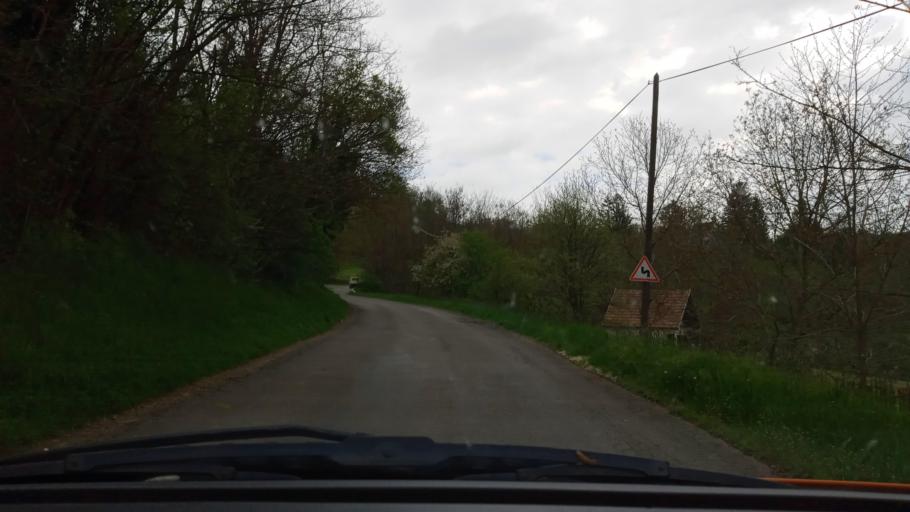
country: HU
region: Baranya
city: Szaszvar
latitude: 46.2685
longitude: 18.3179
